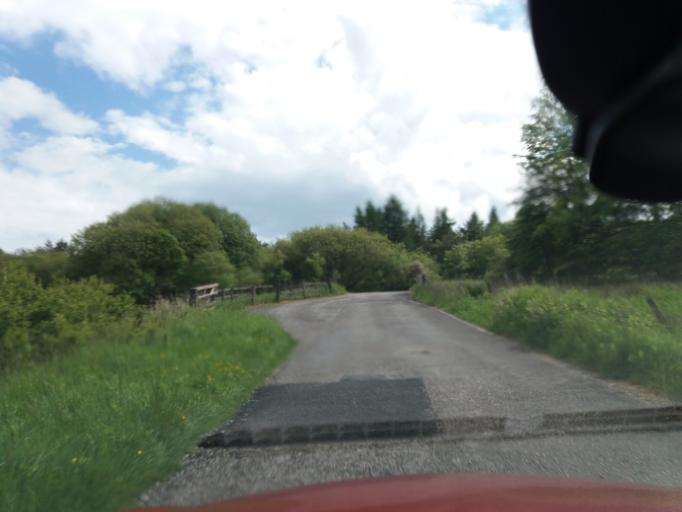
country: GB
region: England
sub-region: Blackburn with Darwen
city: Darwen
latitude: 53.6484
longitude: -2.4242
